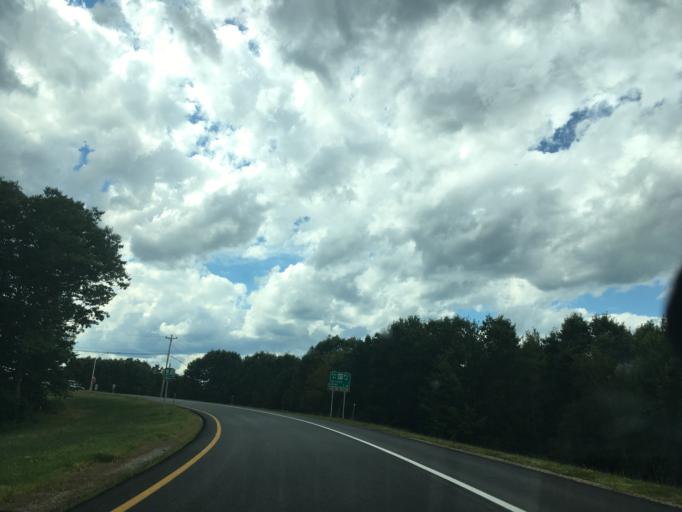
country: US
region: New Hampshire
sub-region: Rockingham County
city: Exeter
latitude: 43.0026
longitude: -70.9751
